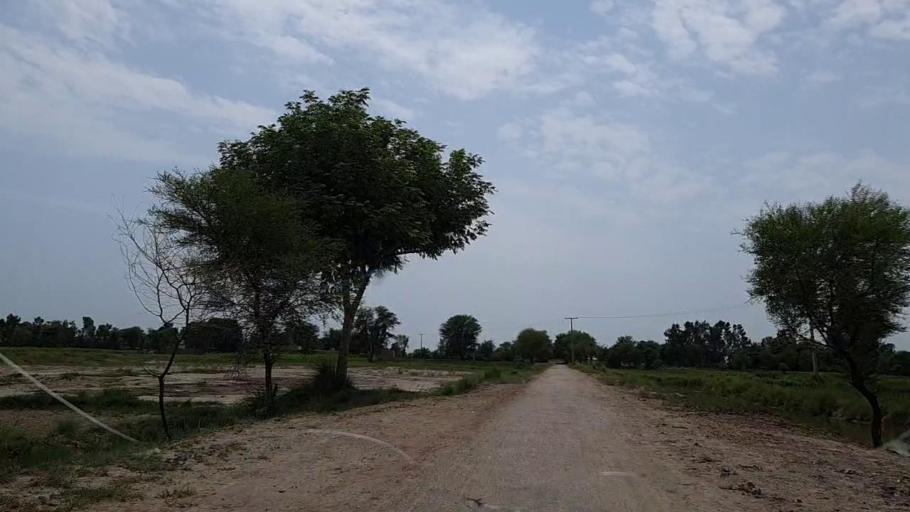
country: PK
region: Sindh
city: Tharu Shah
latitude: 26.9226
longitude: 68.0820
